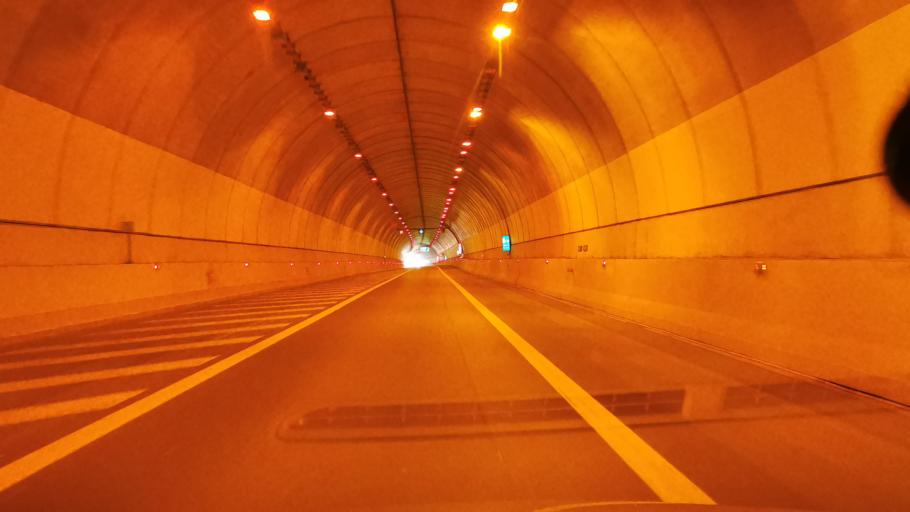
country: IT
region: Piedmont
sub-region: Provincia di Cuneo
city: Cuneo
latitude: 44.4267
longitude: 7.5681
